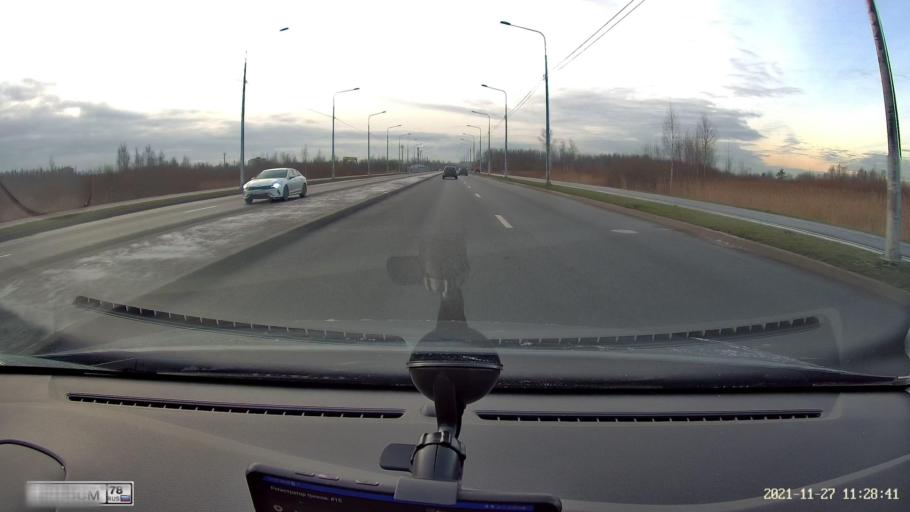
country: RU
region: St.-Petersburg
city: Krasnoye Selo
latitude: 59.7432
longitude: 30.0726
